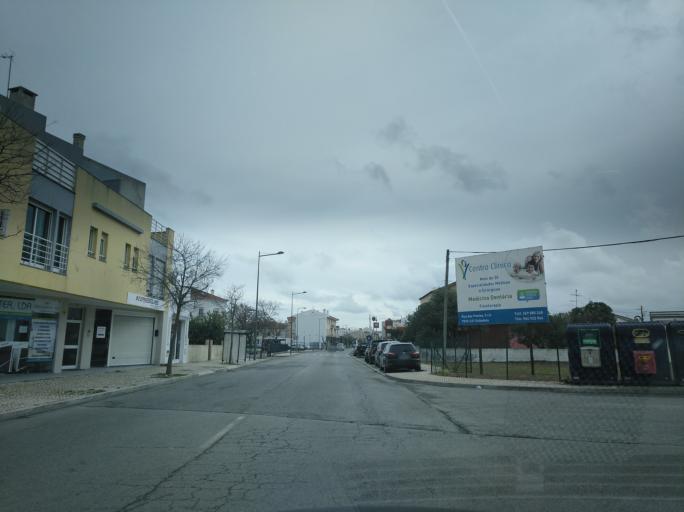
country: PT
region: Setubal
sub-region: Grandola
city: Grandola
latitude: 38.1821
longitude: -8.5672
